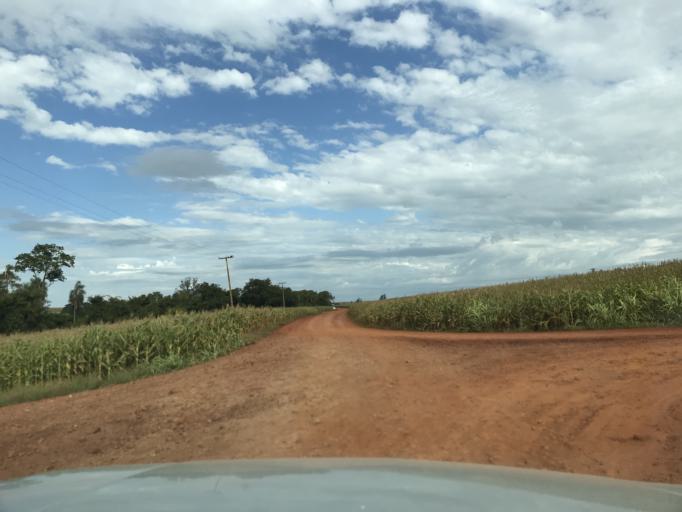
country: BR
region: Parana
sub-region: Palotina
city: Palotina
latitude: -24.3090
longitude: -53.8084
